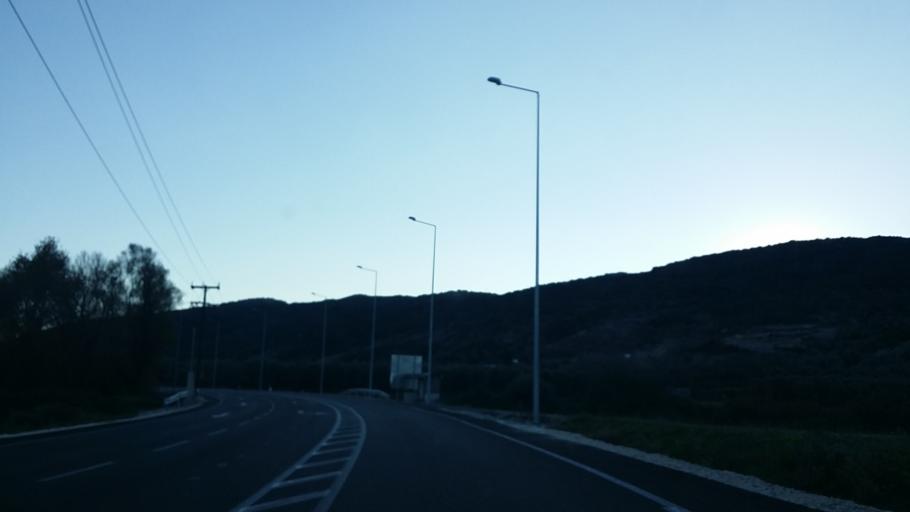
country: GR
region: West Greece
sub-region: Nomos Aitolias kai Akarnanias
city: Lepenou
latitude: 38.7309
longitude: 21.3348
